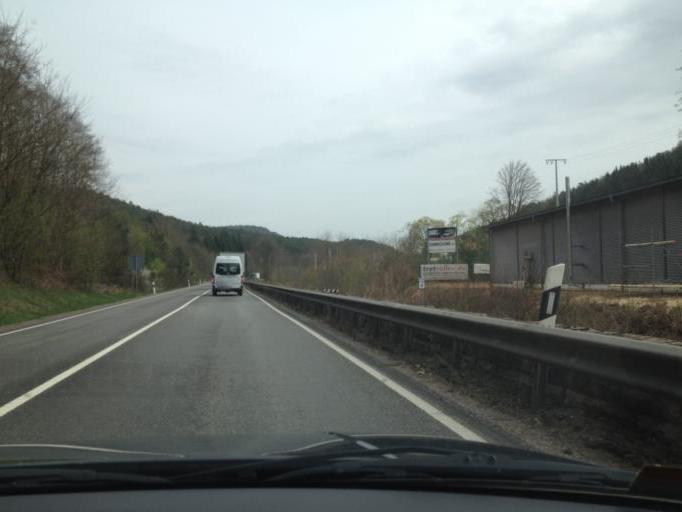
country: DE
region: Rheinland-Pfalz
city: Hauenstein
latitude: 49.2016
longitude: 7.8186
